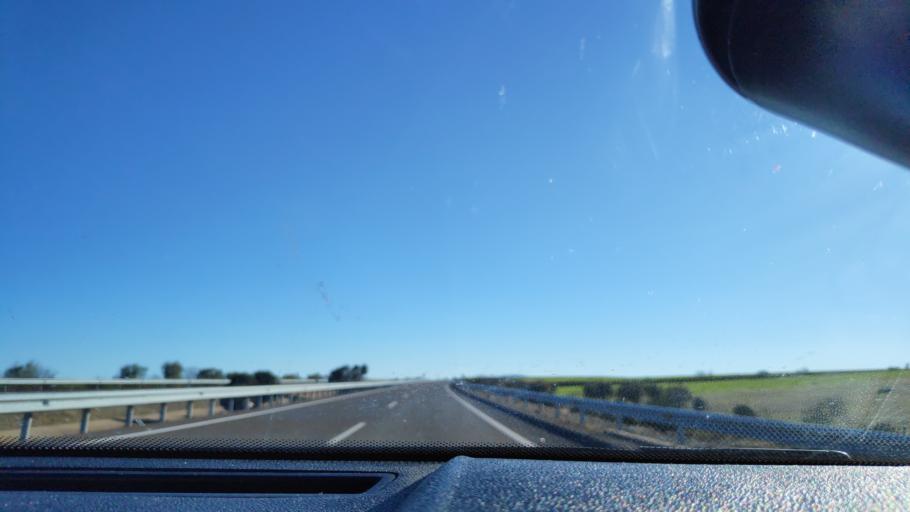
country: ES
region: Extremadura
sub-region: Provincia de Badajoz
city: Fuente de Cantos
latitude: 38.2094
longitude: -6.2870
